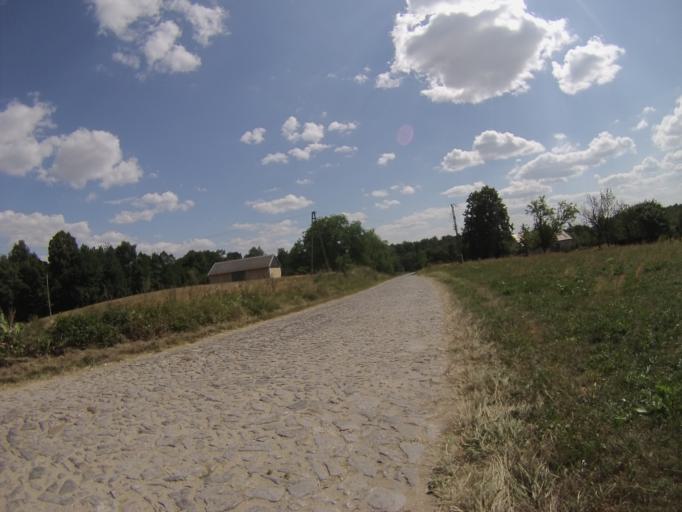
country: PL
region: Swietokrzyskie
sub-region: Powiat kielecki
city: Rakow
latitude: 50.7178
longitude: 21.0789
